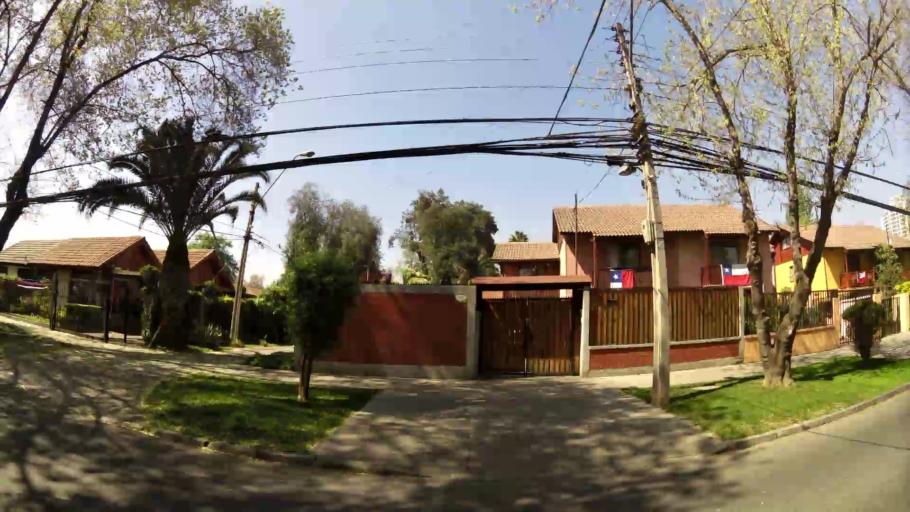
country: CL
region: Santiago Metropolitan
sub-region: Provincia de Santiago
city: Villa Presidente Frei, Nunoa, Santiago, Chile
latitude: -33.4512
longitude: -70.5764
